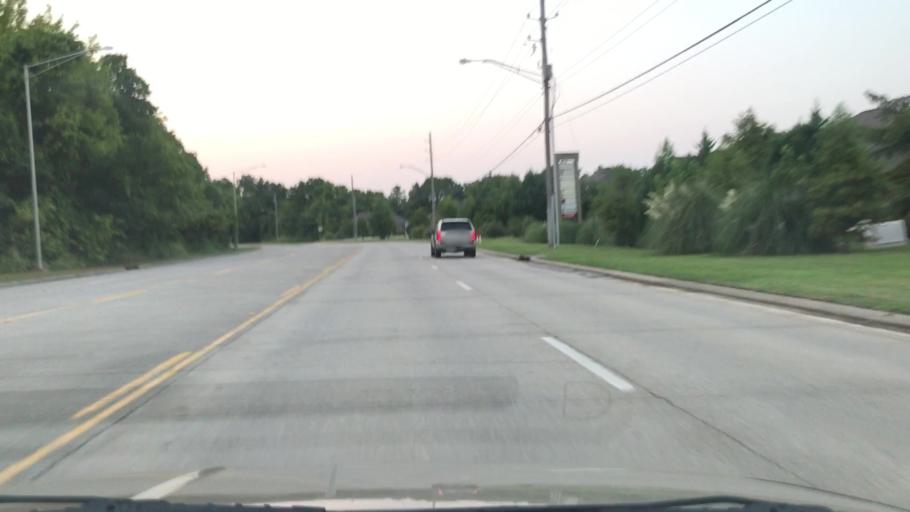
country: US
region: Louisiana
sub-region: Bossier Parish
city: Bossier City
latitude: 32.4324
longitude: -93.7260
